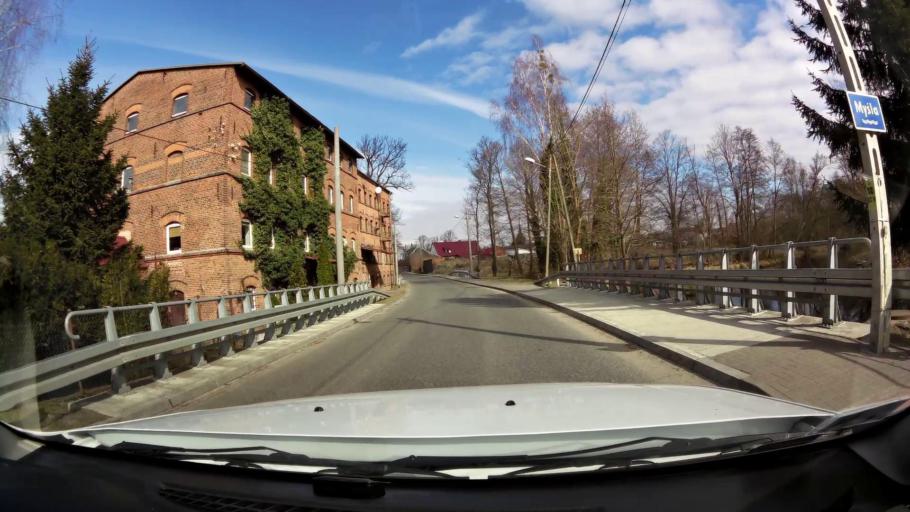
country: PL
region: West Pomeranian Voivodeship
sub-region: Powiat mysliborski
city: Debno
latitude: 52.7040
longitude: 14.6473
